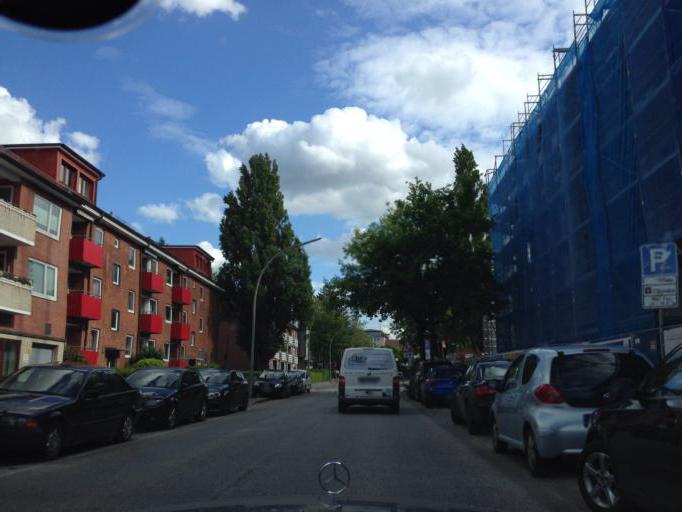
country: DE
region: Hamburg
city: Marienthal
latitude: 53.5739
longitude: 10.0632
